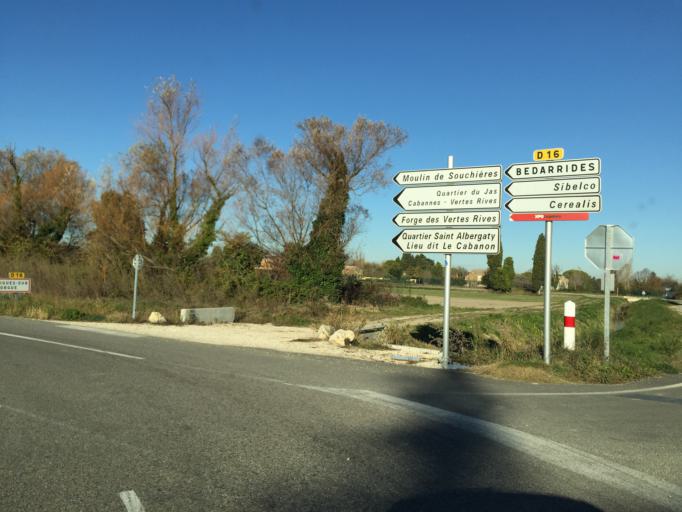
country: FR
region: Provence-Alpes-Cote d'Azur
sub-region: Departement du Vaucluse
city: Althen-des-Paluds
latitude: 44.0099
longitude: 4.9378
